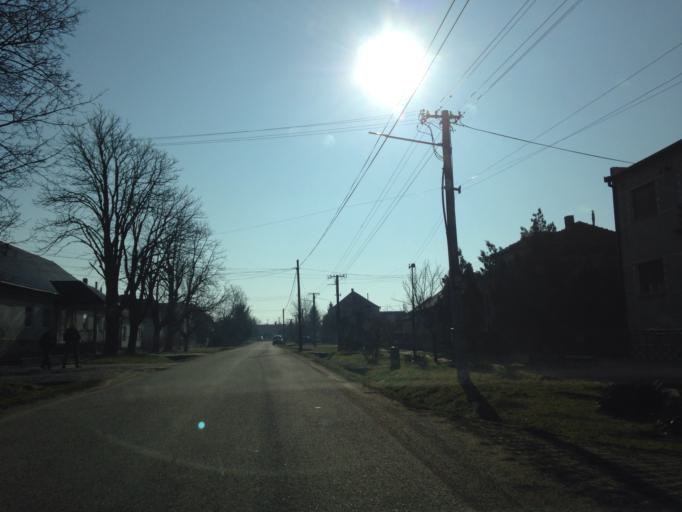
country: SK
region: Nitriansky
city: Svodin
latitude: 47.9277
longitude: 18.4009
